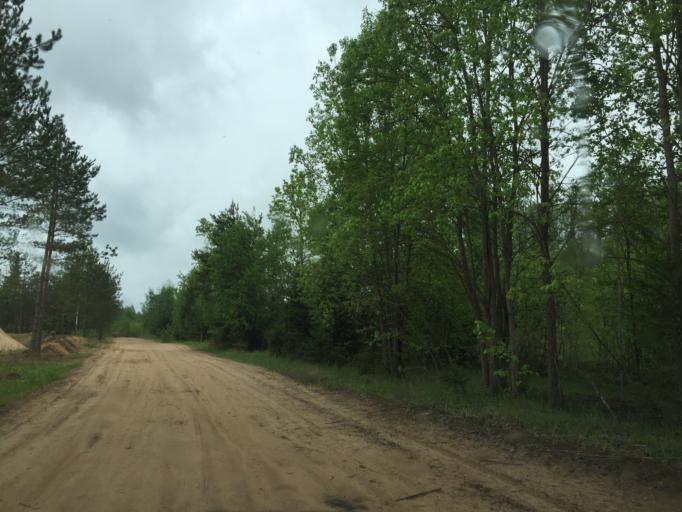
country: LV
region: Kegums
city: Kegums
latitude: 56.7375
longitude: 24.7632
